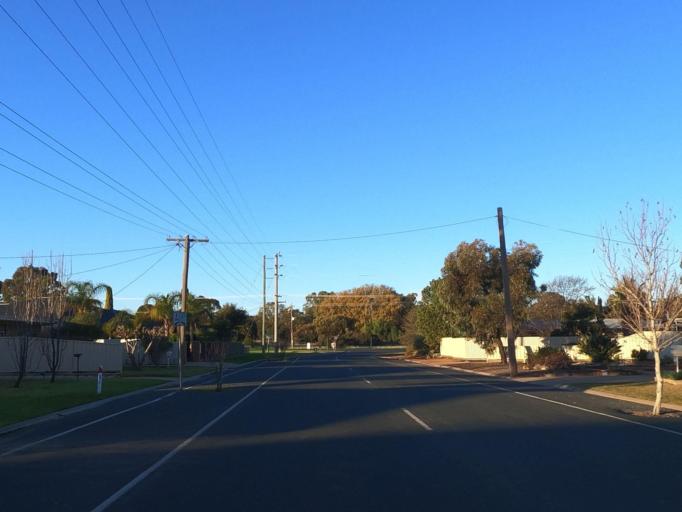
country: AU
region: Victoria
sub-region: Swan Hill
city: Swan Hill
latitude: -35.3590
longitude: 143.5610
